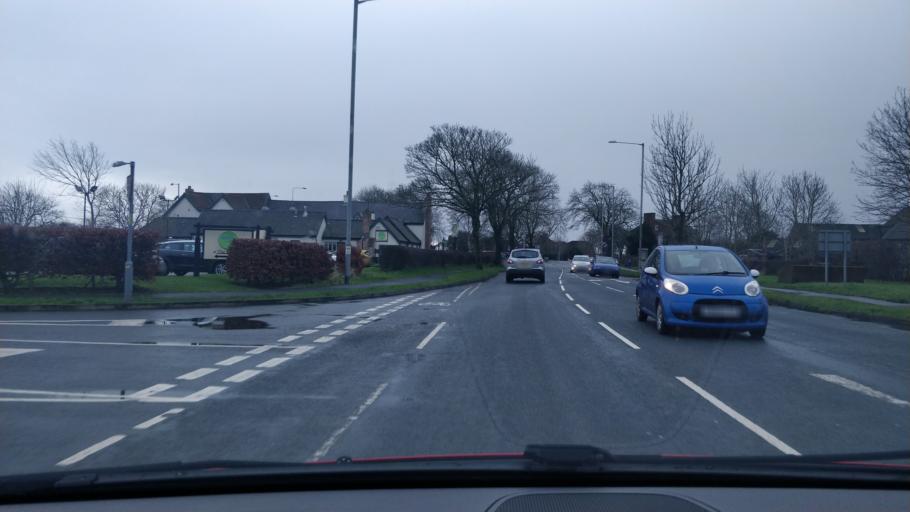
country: GB
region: England
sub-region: Lancashire
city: Tarleton
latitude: 53.7085
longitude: -2.7936
